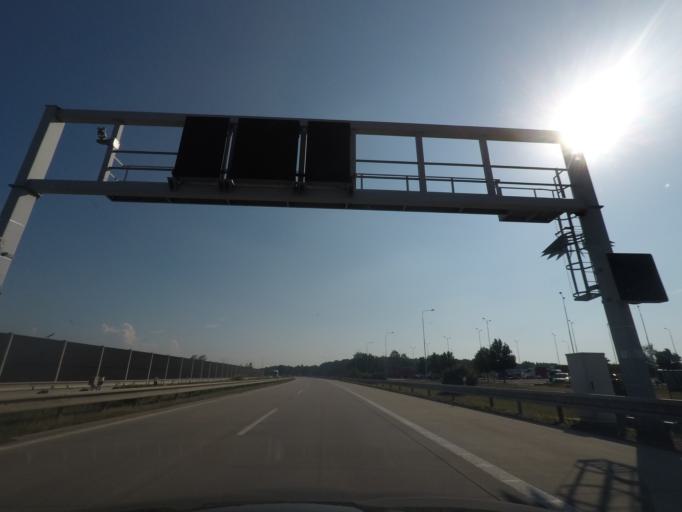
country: PL
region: Silesian Voivodeship
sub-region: Powiat raciborski
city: Chalupki
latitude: 49.9050
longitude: 18.3086
